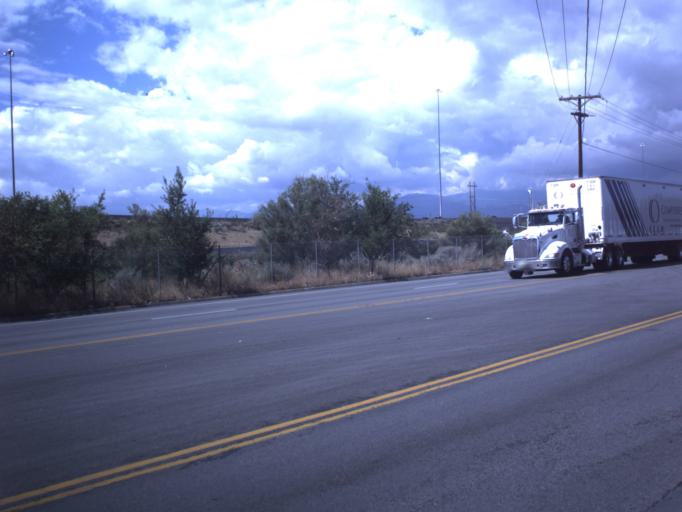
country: US
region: Utah
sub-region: Salt Lake County
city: South Salt Lake
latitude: 40.7257
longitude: -111.9133
